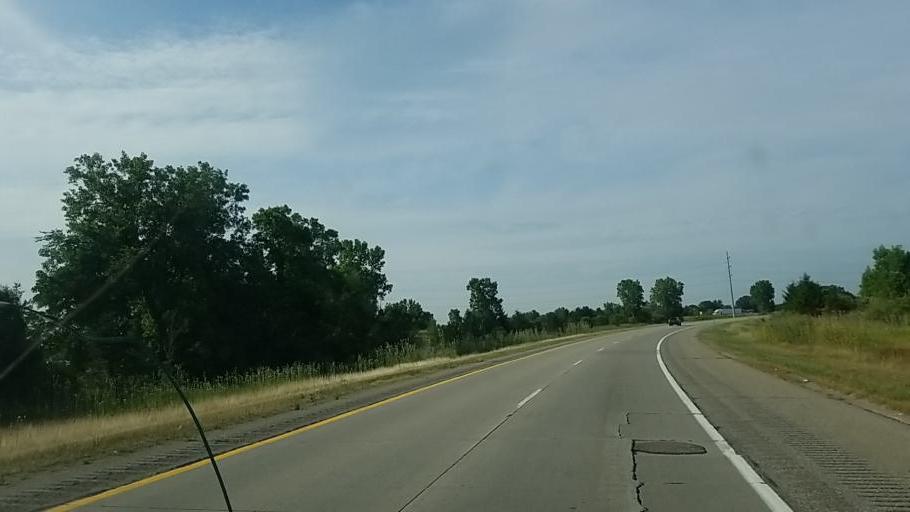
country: US
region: Michigan
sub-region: Eaton County
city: Dimondale
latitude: 42.6913
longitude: -84.6689
